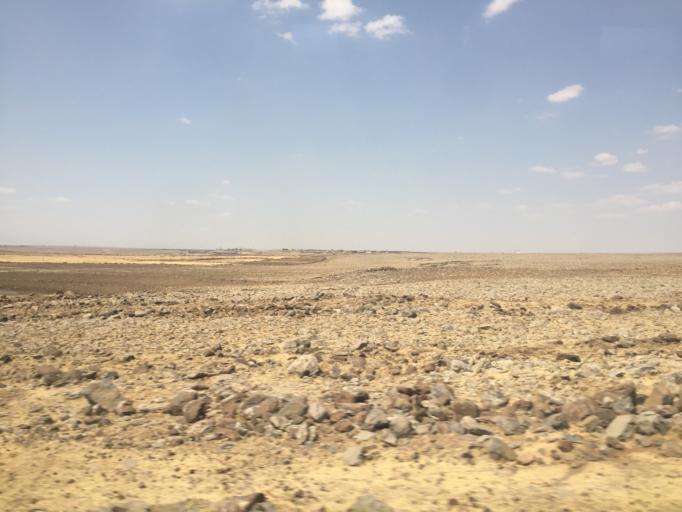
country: TR
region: Sanliurfa
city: Siverek
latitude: 37.7764
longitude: 39.4581
